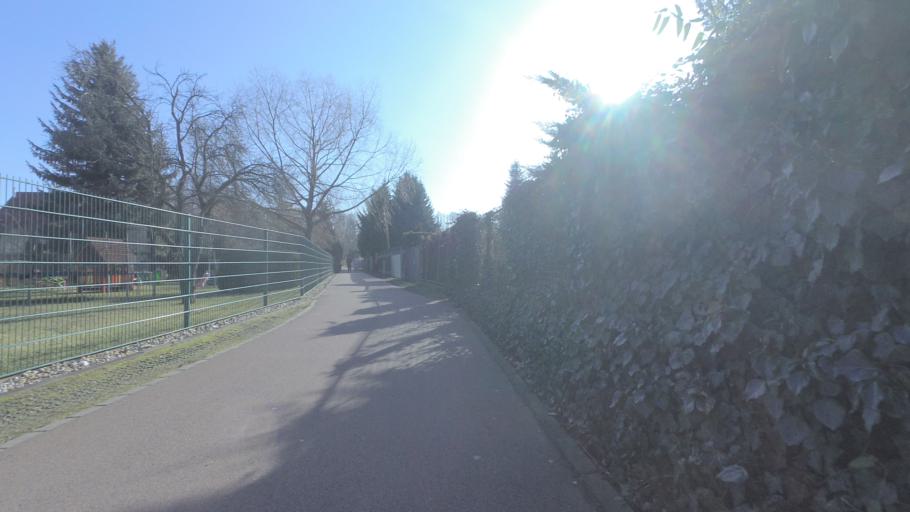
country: DE
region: Brandenburg
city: Luckenwalde
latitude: 52.0847
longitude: 13.1717
